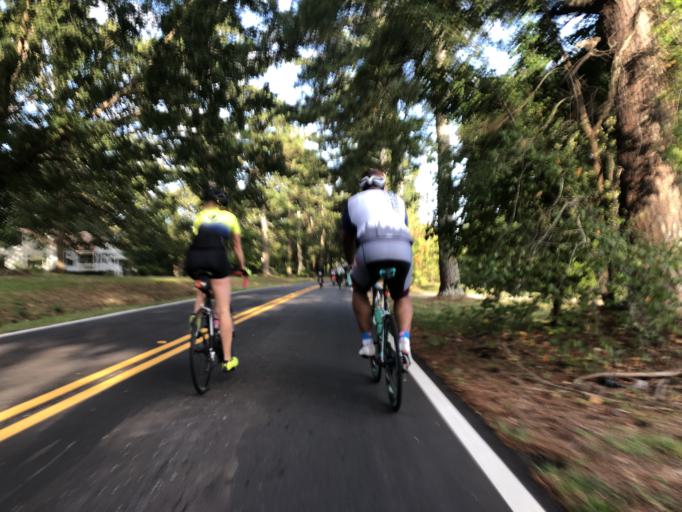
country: US
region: Georgia
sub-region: Fulton County
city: Palmetto
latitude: 33.5729
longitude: -84.6655
